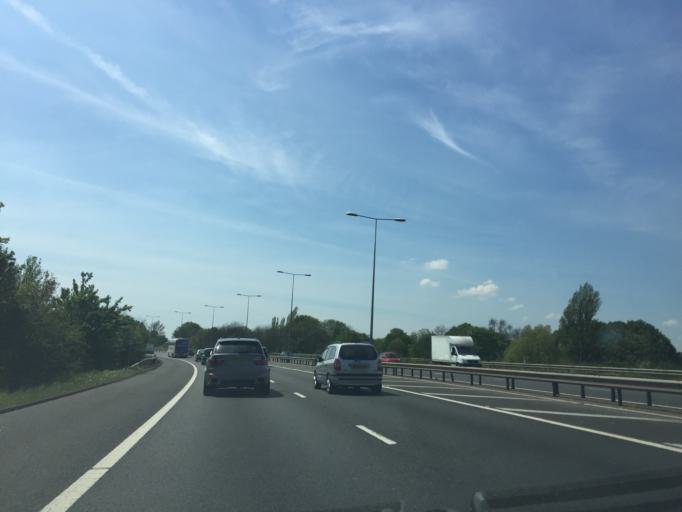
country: GB
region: England
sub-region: Essex
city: Buckhurst Hill
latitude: 51.6116
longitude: 0.0512
